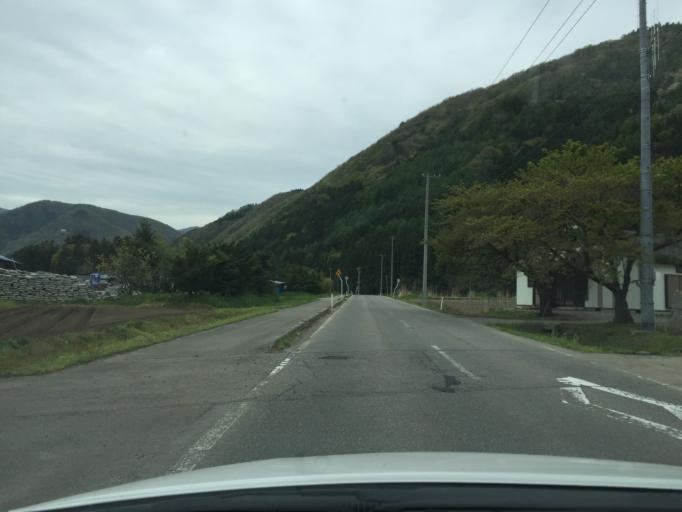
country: JP
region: Fukushima
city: Inawashiro
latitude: 37.5941
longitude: 140.1401
